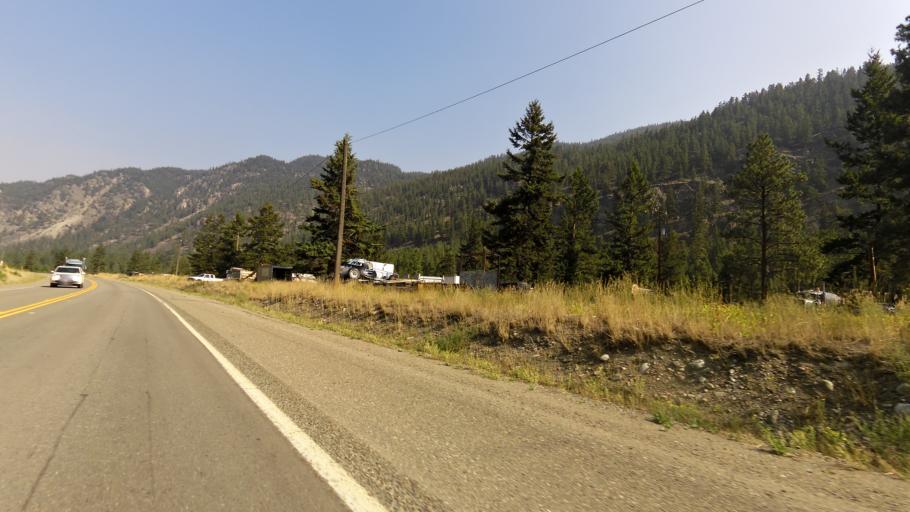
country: CA
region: British Columbia
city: Princeton
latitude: 49.3927
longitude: -120.2088
